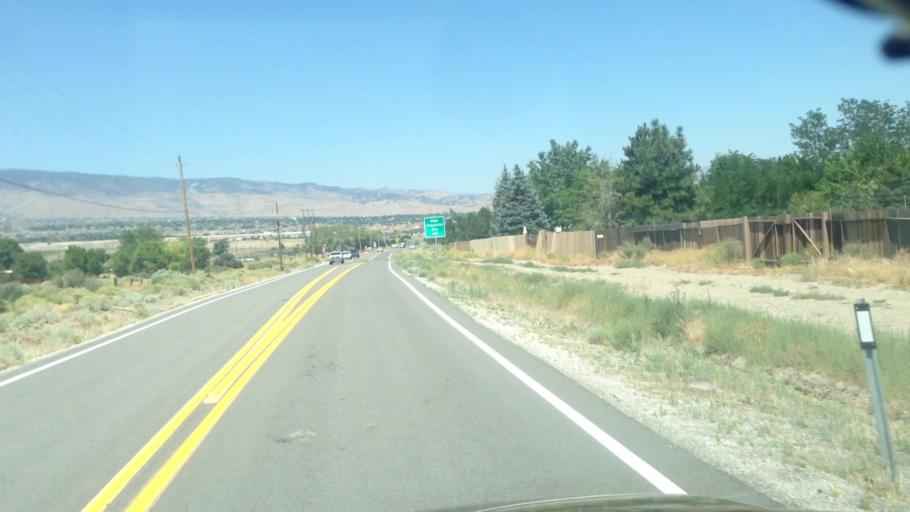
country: US
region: Nevada
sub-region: Storey County
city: Virginia City
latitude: 39.3953
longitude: -119.7308
